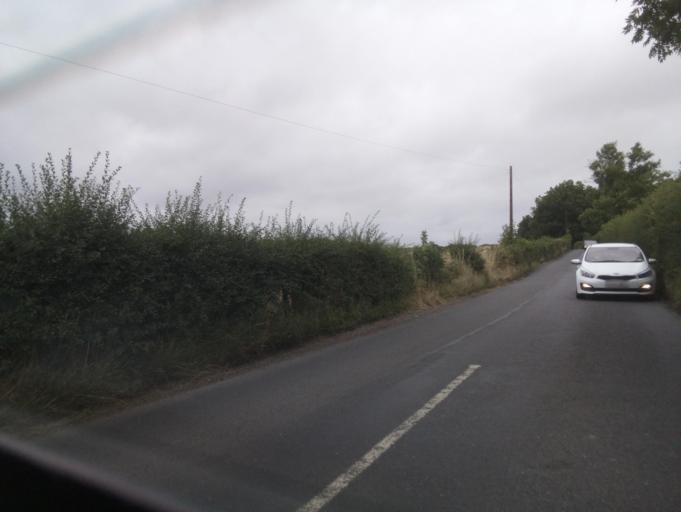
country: GB
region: England
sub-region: Derbyshire
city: Swadlincote
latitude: 52.7941
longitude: -1.5373
